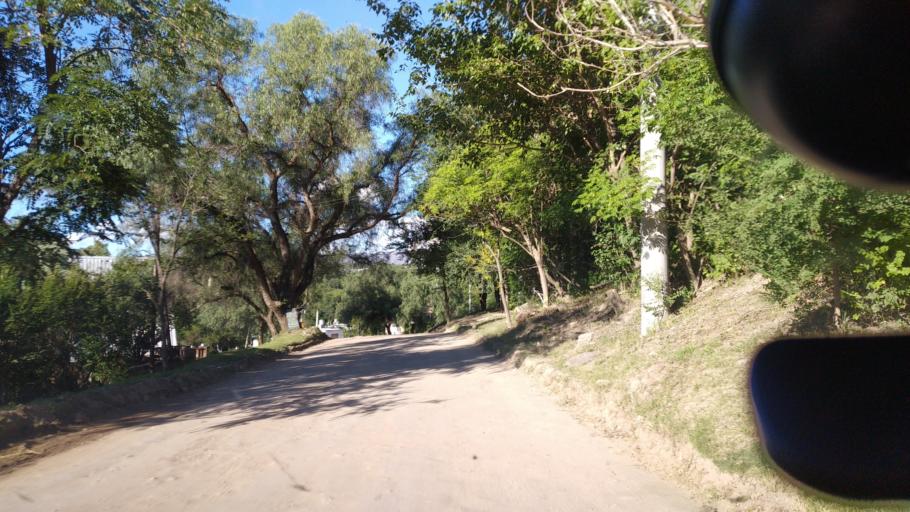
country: AR
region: Cordoba
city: Mina Clavero
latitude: -31.7278
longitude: -64.9978
